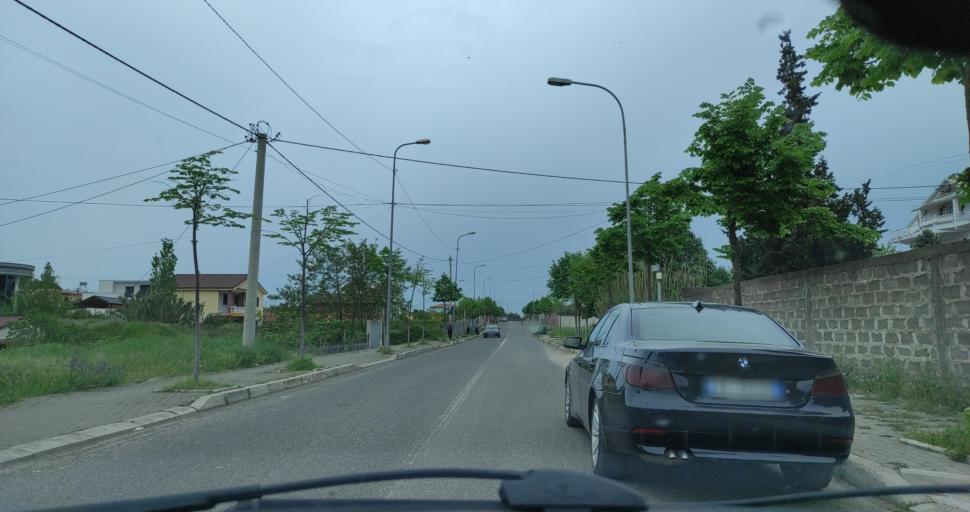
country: AL
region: Lezhe
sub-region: Rrethi i Kurbinit
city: Mamurras
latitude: 41.5845
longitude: 19.6932
